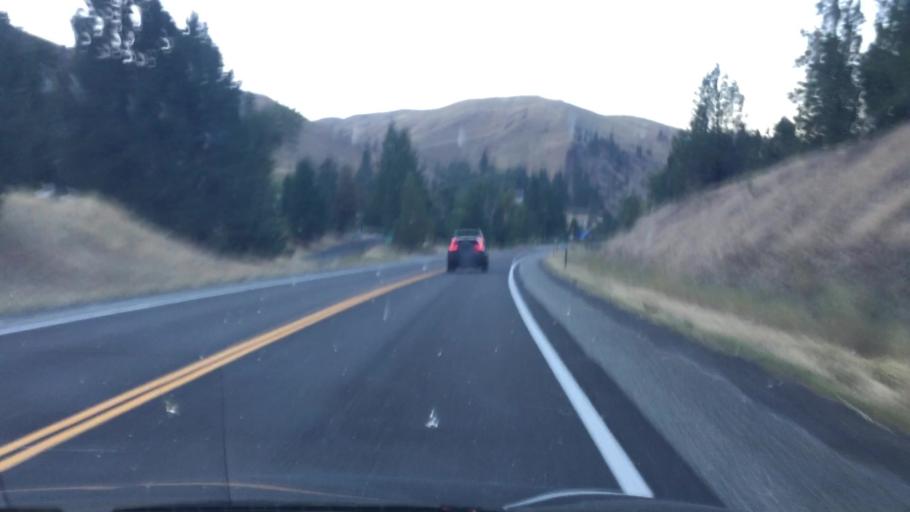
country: US
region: Idaho
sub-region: Valley County
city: McCall
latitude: 45.3036
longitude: -116.3622
